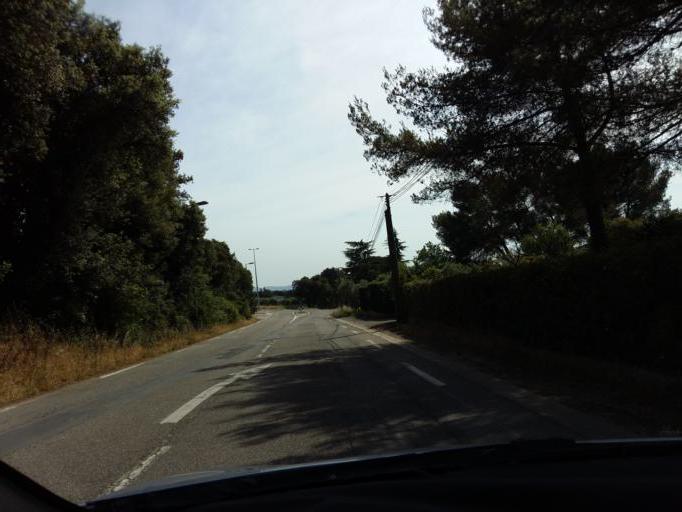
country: FR
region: Provence-Alpes-Cote d'Azur
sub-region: Departement du Vaucluse
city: Cavaillon
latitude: 43.8480
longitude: 5.0200
